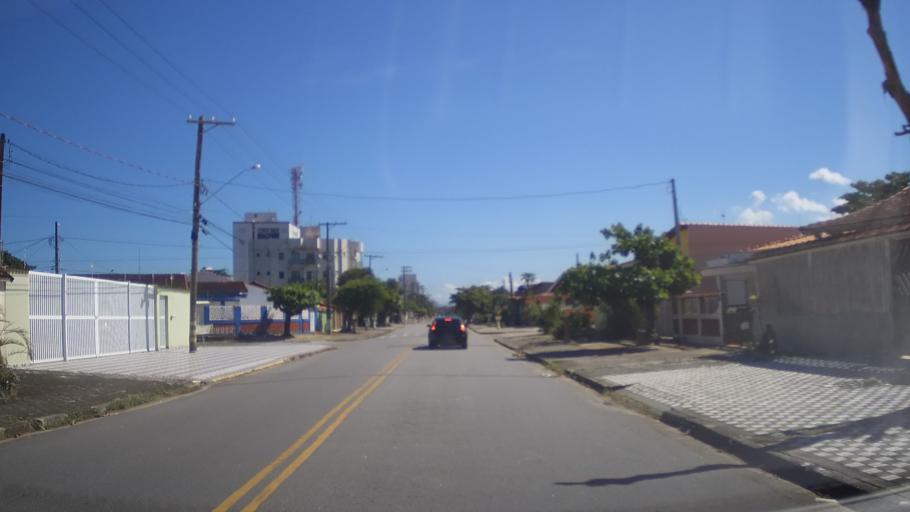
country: BR
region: Sao Paulo
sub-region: Mongagua
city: Mongagua
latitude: -24.1286
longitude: -46.6860
